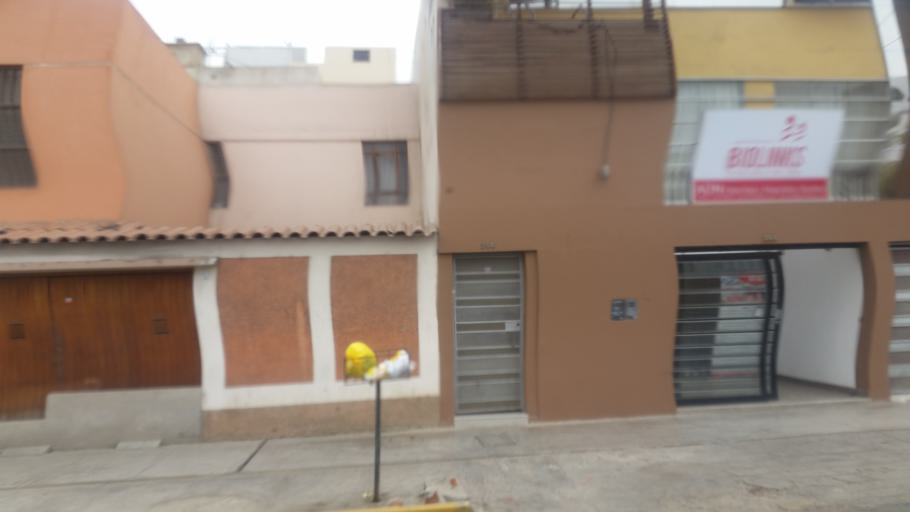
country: PE
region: La Libertad
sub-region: Provincia de Trujillo
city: Trujillo
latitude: -8.1131
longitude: -79.0338
